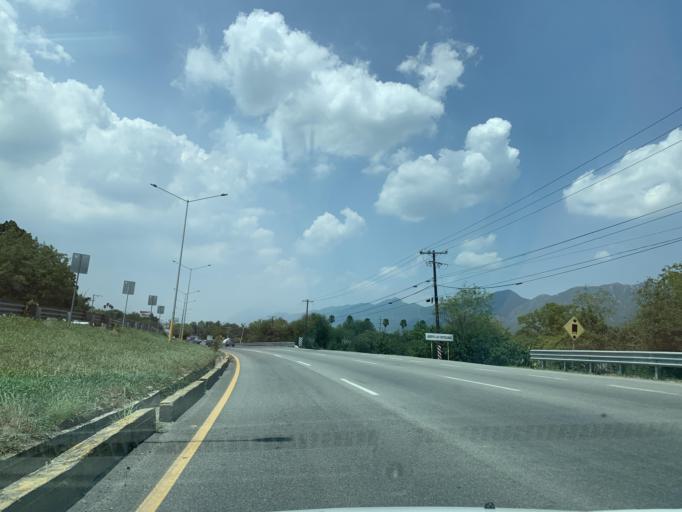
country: MX
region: Nuevo Leon
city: Santiago
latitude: 25.4395
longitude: -100.1535
